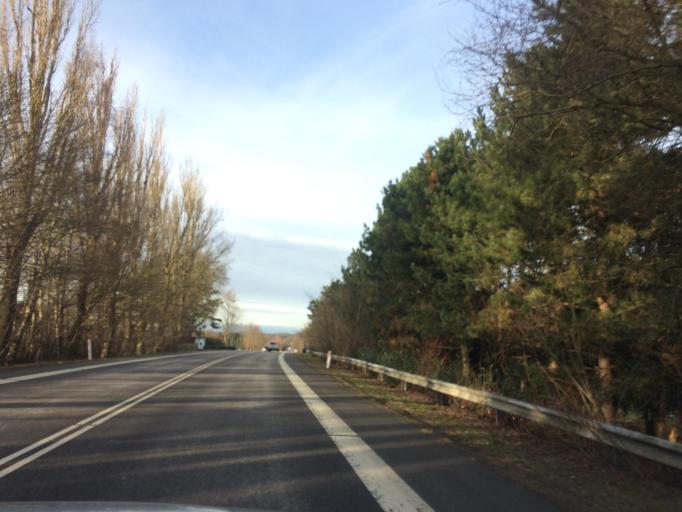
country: DK
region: Capital Region
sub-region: Fredensborg Kommune
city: Kokkedal
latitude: 55.9237
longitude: 12.4457
